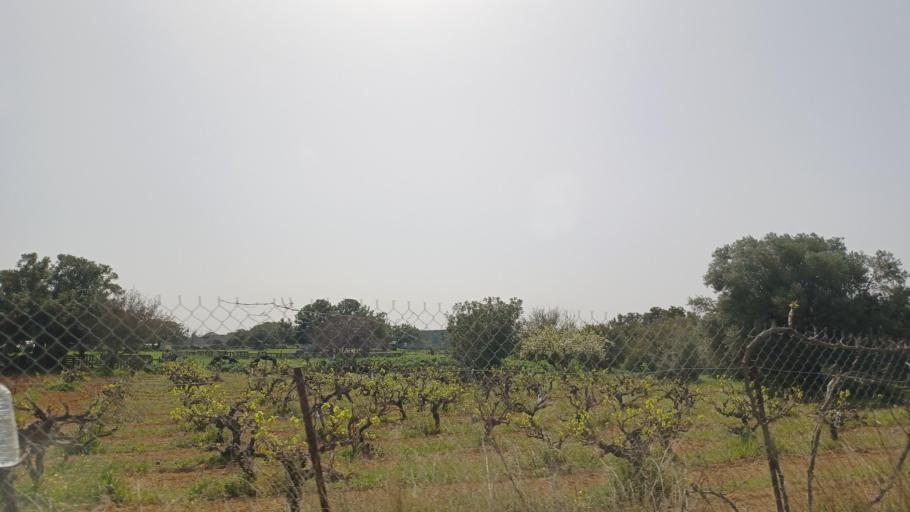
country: CY
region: Limassol
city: Pissouri
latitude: 34.7276
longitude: 32.7287
